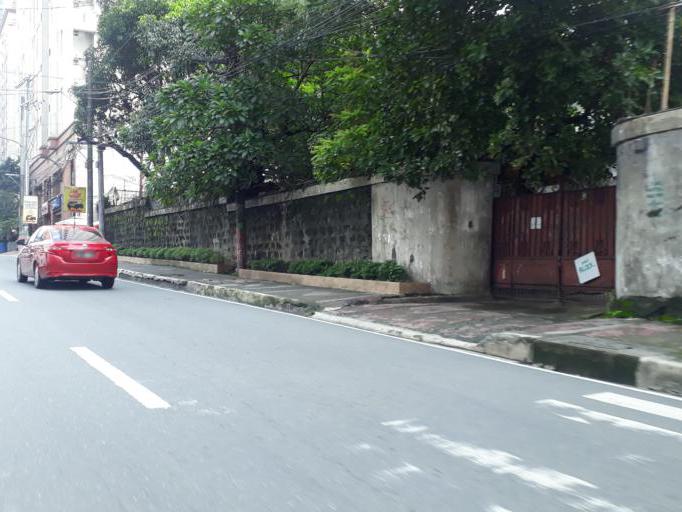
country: PH
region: Metro Manila
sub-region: San Juan
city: San Juan
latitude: 14.6104
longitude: 121.0366
